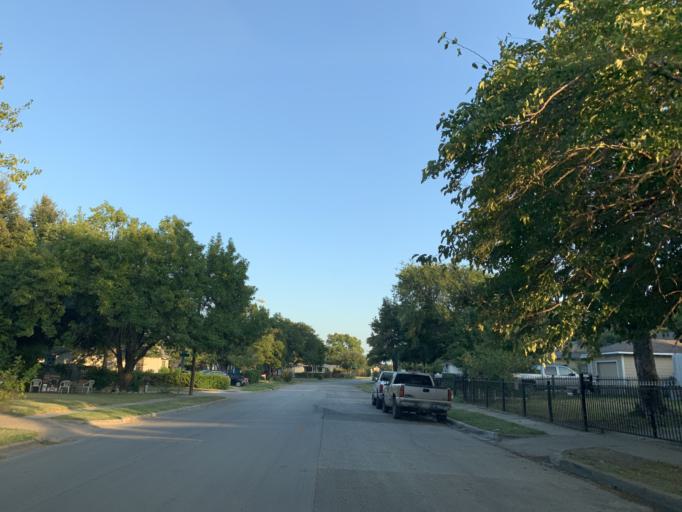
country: US
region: Texas
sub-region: Dallas County
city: Hutchins
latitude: 32.7012
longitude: -96.7708
